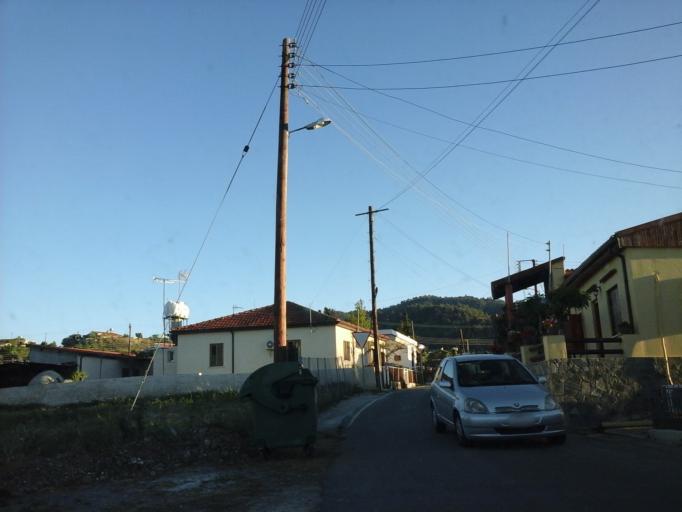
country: CY
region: Lefkosia
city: Astromeritis
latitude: 35.0705
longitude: 32.9921
